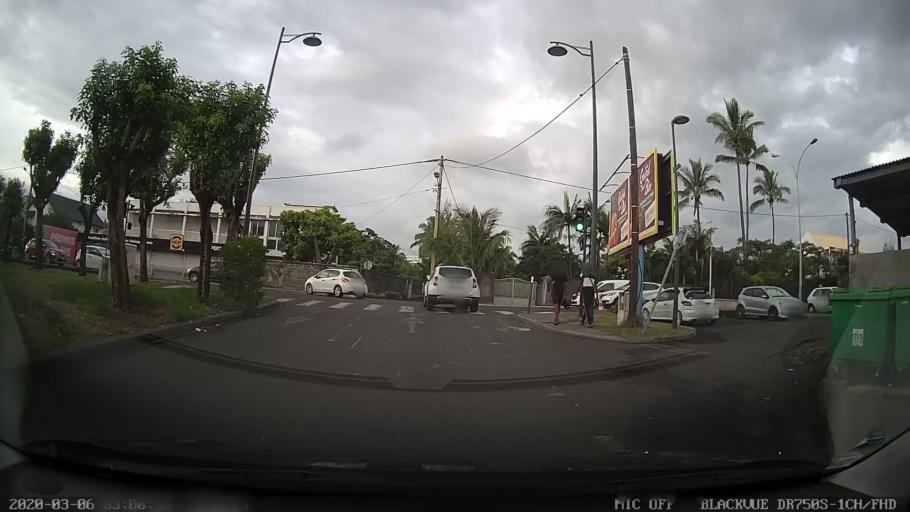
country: RE
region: Reunion
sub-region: Reunion
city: Saint-Pierre
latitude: -21.3355
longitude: 55.4649
